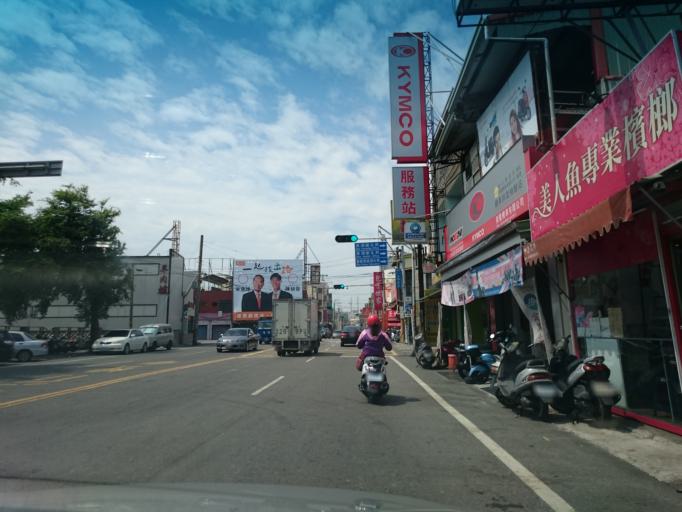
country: TW
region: Taiwan
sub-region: Changhua
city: Chang-hua
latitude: 23.9576
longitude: 120.4835
